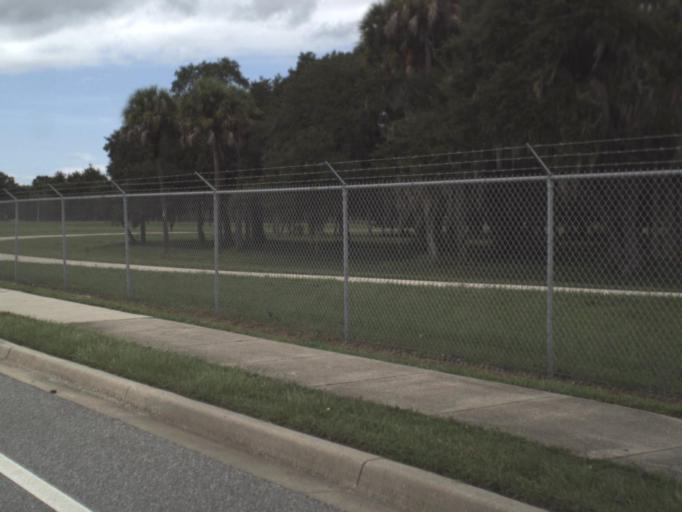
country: US
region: Florida
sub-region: Sarasota County
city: North Sarasota
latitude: 27.3832
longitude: -82.5429
